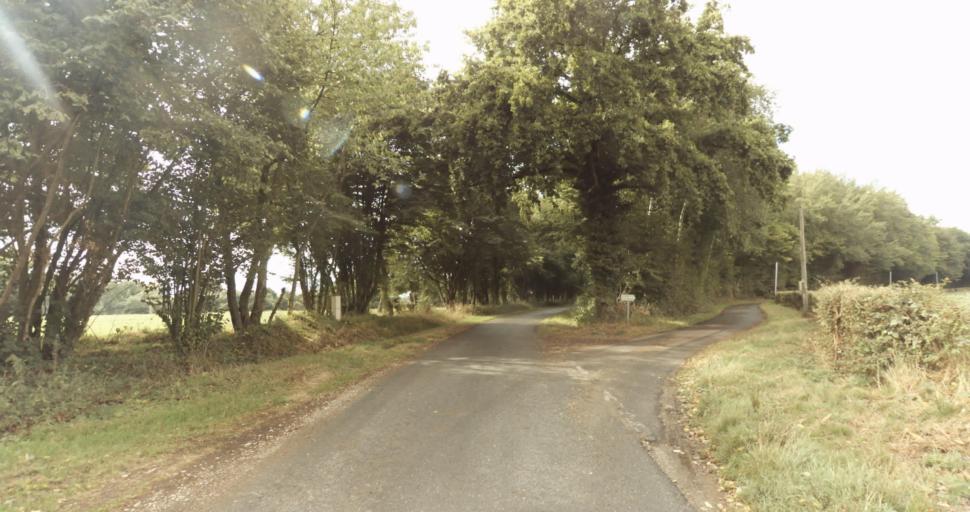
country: FR
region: Lower Normandy
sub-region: Departement de l'Orne
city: Vimoutiers
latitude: 48.8567
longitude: 0.1714
